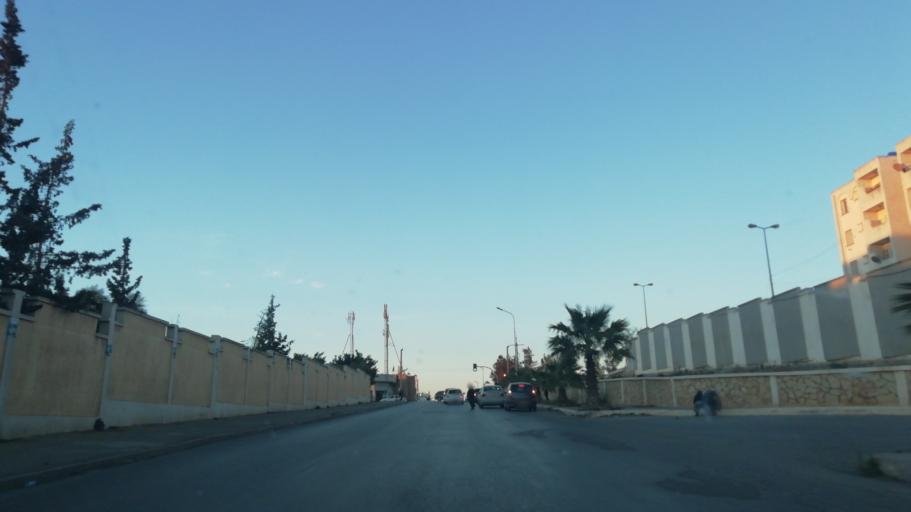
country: DZ
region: Oran
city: Bir el Djir
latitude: 35.7011
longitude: -0.5853
